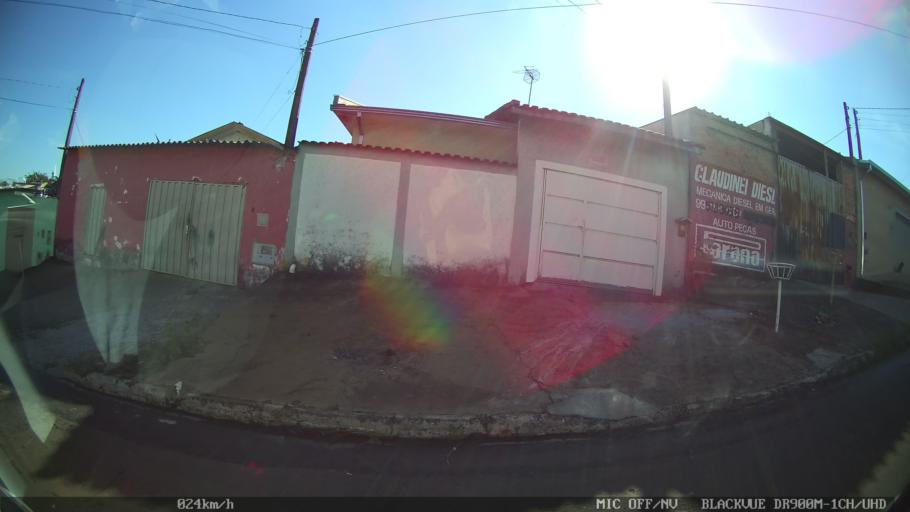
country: BR
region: Sao Paulo
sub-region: Franca
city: Franca
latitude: -20.4908
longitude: -47.4157
